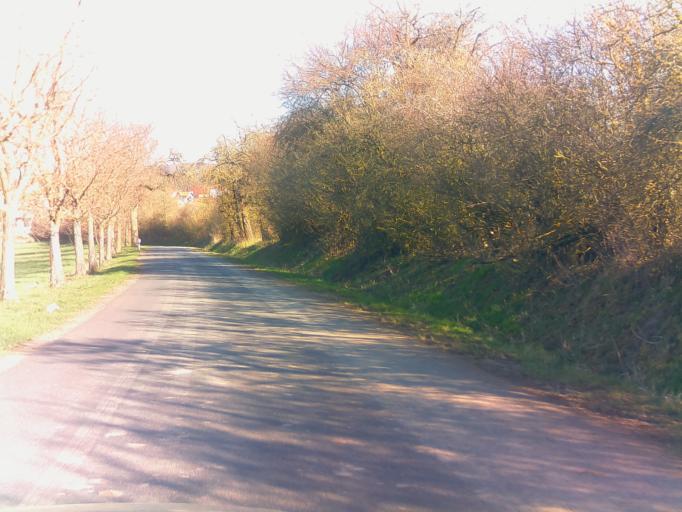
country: DE
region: Thuringia
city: Henneberg
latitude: 50.5040
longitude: 10.3089
